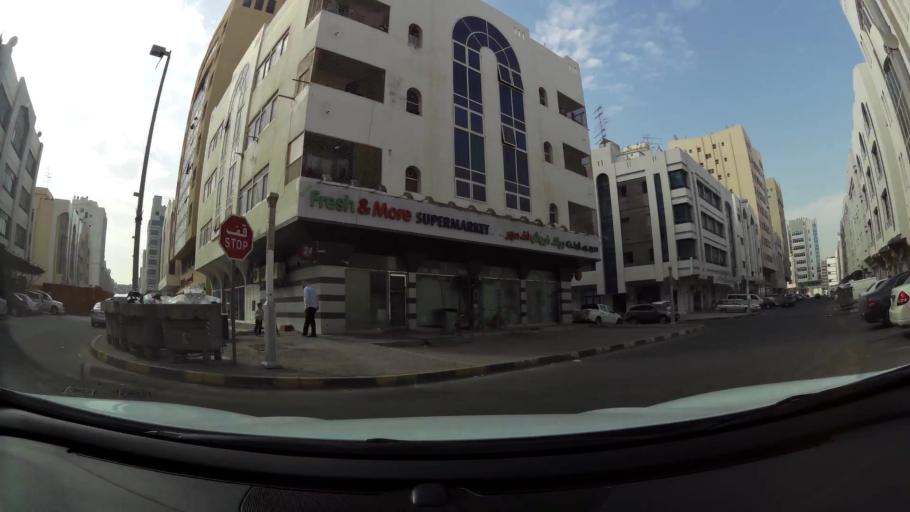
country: AE
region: Abu Dhabi
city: Abu Dhabi
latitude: 24.3226
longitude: 54.5386
